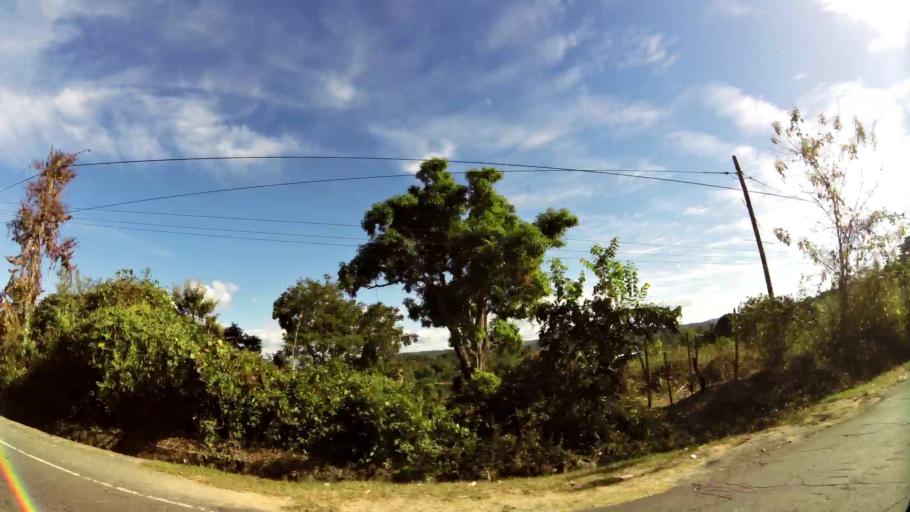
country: SV
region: Cuscatlan
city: Tenancingo
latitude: 13.8306
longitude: -89.0311
